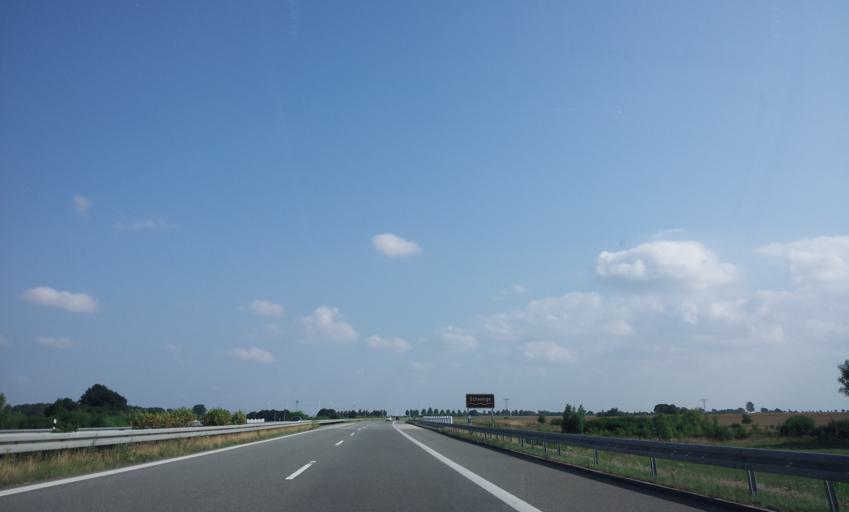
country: DE
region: Mecklenburg-Vorpommern
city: Dersekow
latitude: 54.0330
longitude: 13.2741
